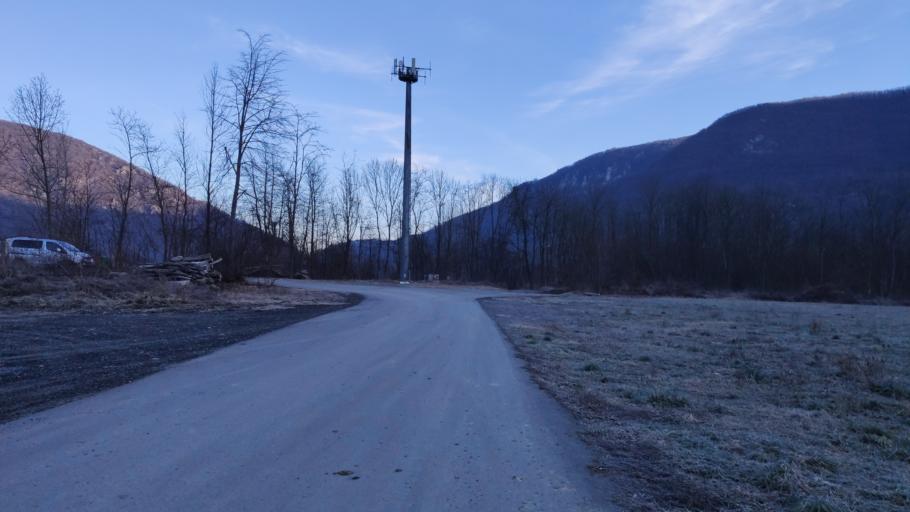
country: IT
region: Piedmont
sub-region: Provincia di Cuneo
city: Priola
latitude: 44.2618
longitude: 8.0288
